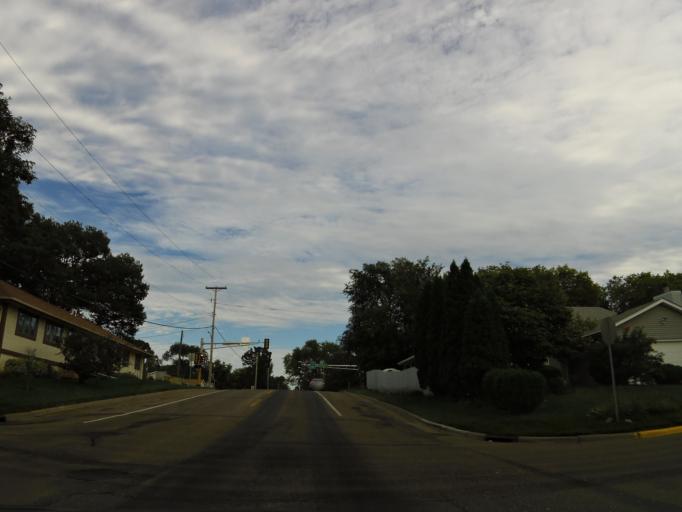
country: US
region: Minnesota
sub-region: Anoka County
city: Columbia Heights
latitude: 45.0482
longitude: -93.2643
